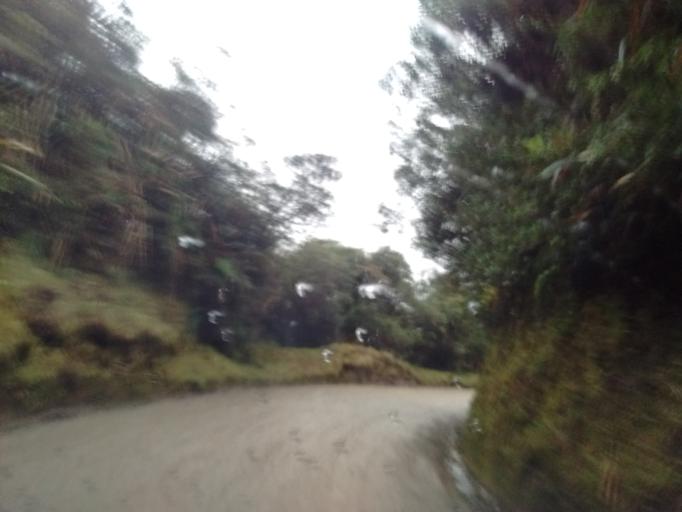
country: CO
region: Cauca
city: Paispamba
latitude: 2.1637
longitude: -76.4011
